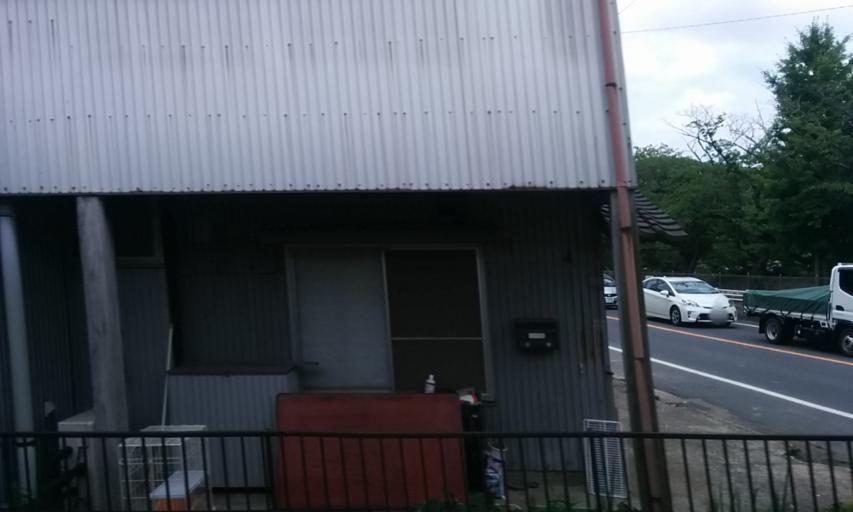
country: JP
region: Chiba
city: Katori-shi
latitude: 35.8976
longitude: 140.4897
